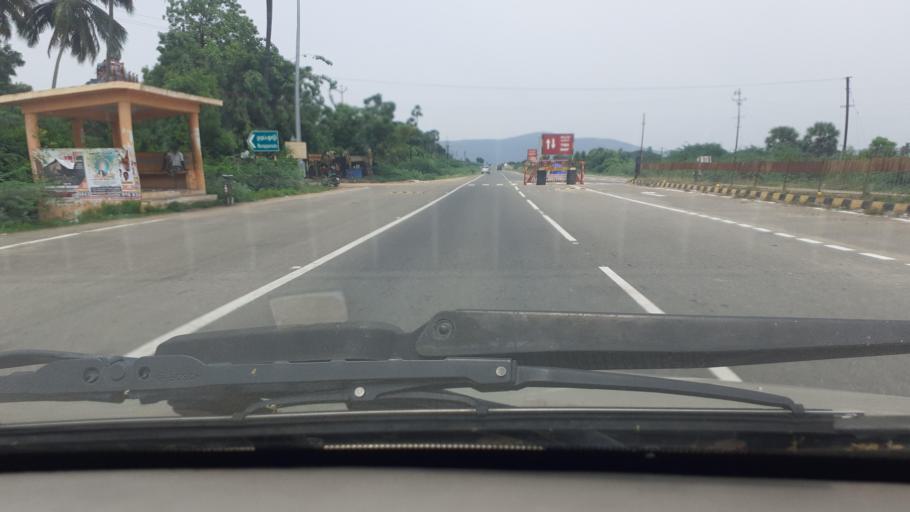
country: IN
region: Tamil Nadu
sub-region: Thoothukkudi
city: Srivaikuntam
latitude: 8.7121
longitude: 77.8295
